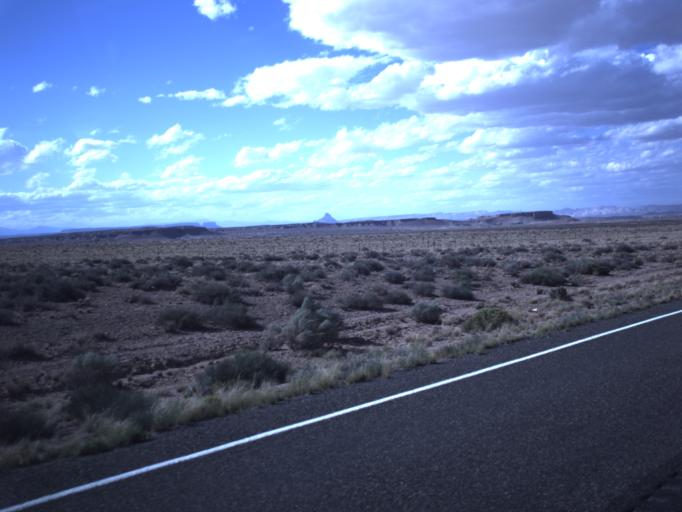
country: US
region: Utah
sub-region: Emery County
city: Ferron
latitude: 38.2853
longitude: -110.6639
